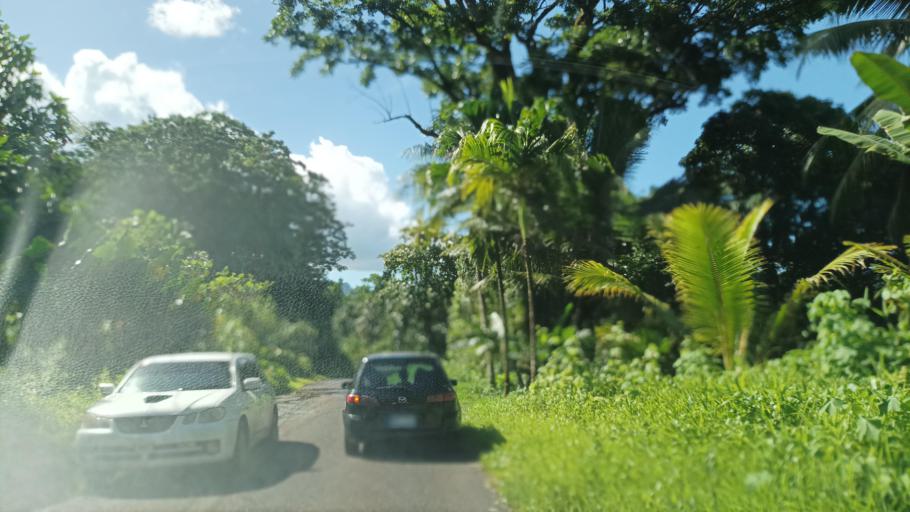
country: FM
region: Pohnpei
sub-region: Madolenihm Municipality
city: Madolenihm Municipality Government
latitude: 6.8642
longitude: 158.2919
